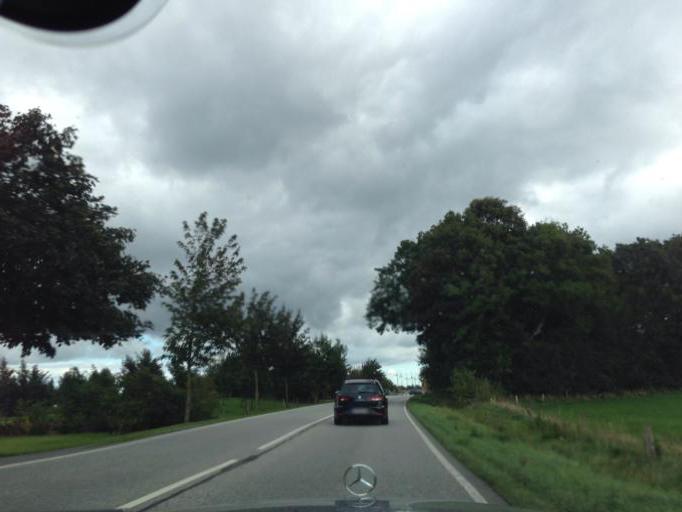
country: DE
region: Schleswig-Holstein
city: Stadum
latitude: 54.7430
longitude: 9.0481
